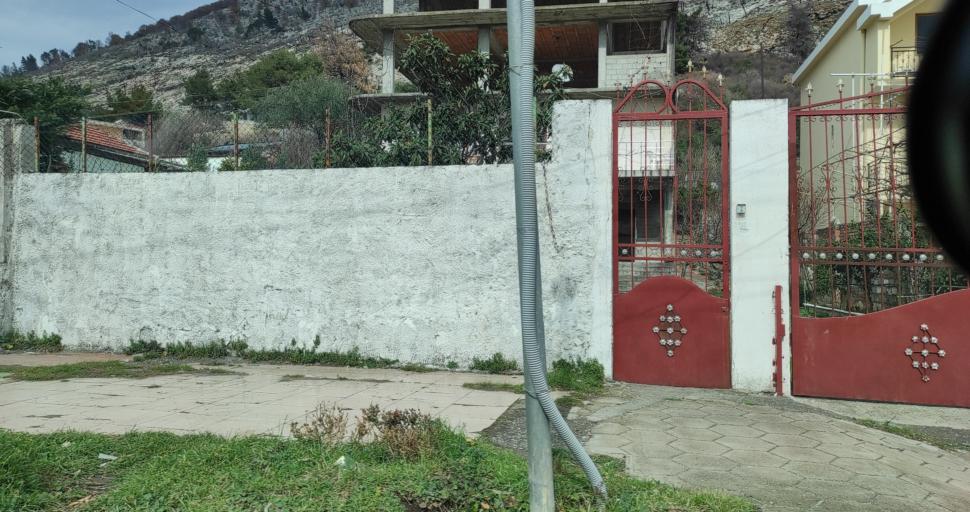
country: AL
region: Lezhe
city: Shengjin
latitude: 41.8150
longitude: 19.5902
